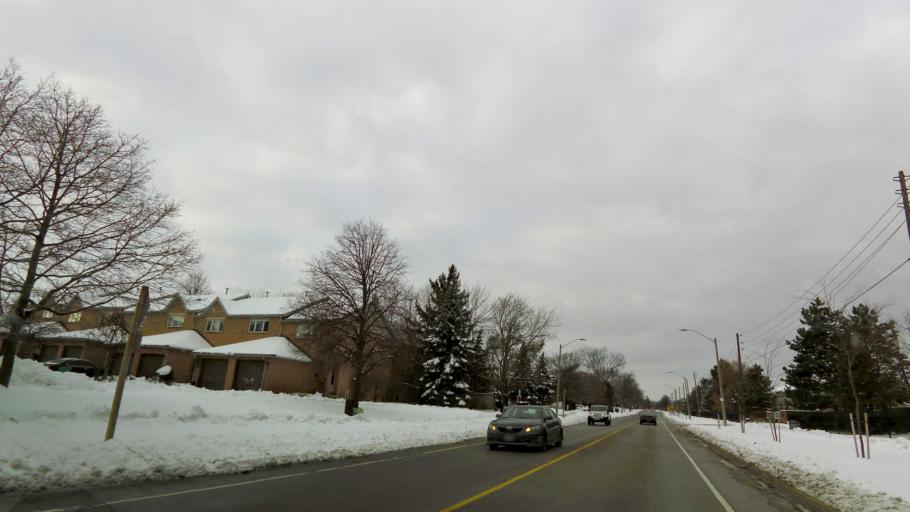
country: CA
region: Ontario
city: Mississauga
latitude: 43.5370
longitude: -79.6698
